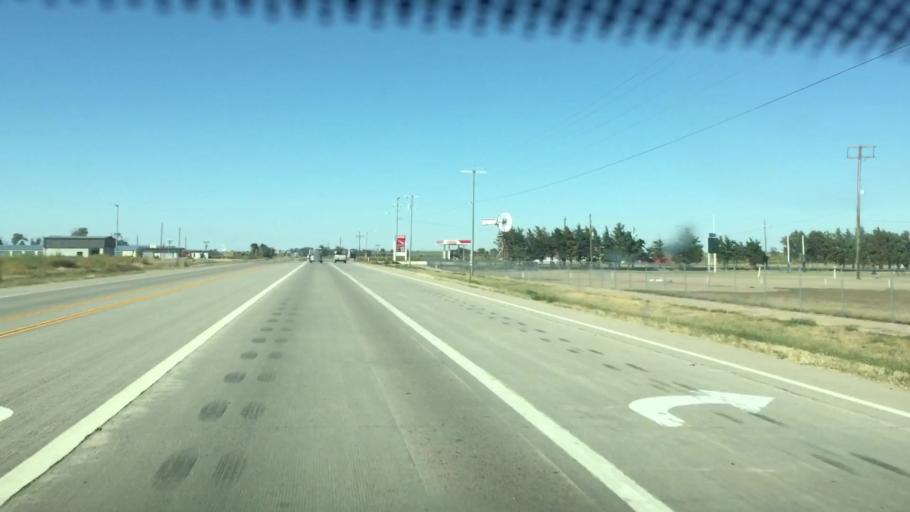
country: US
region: Colorado
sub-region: Prowers County
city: Lamar
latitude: 38.1562
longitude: -102.7236
